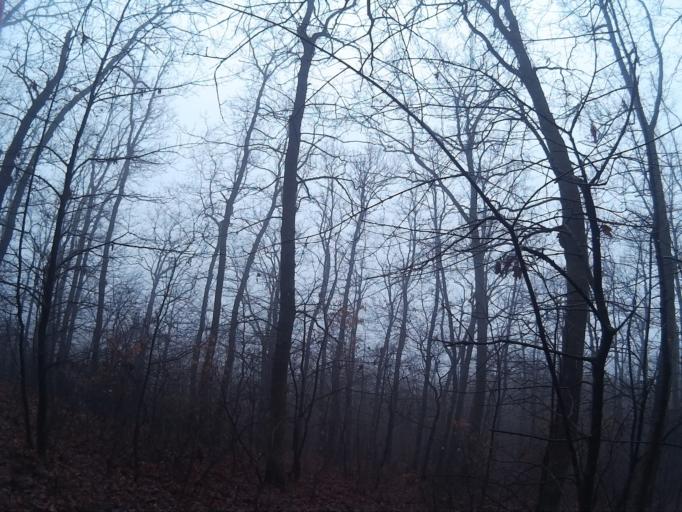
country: HU
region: Nograd
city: Somoskoujfalu
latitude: 48.1385
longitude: 19.8496
